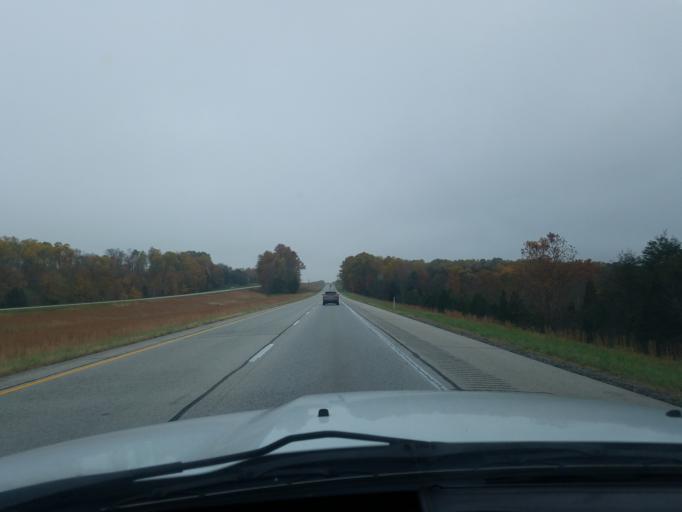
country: US
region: Indiana
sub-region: Floyd County
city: Georgetown
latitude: 38.2540
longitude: -86.0331
